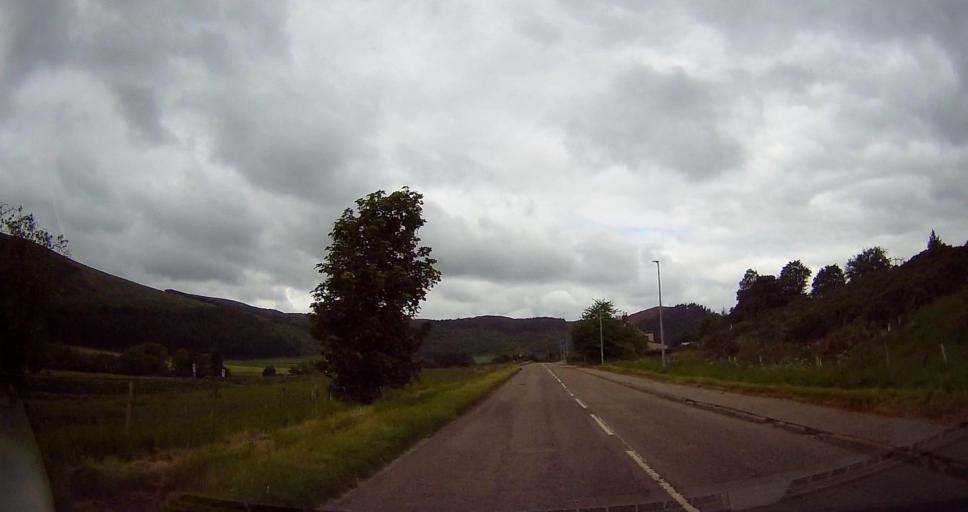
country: GB
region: Scotland
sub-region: Highland
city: Dornoch
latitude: 57.9899
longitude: -4.1582
